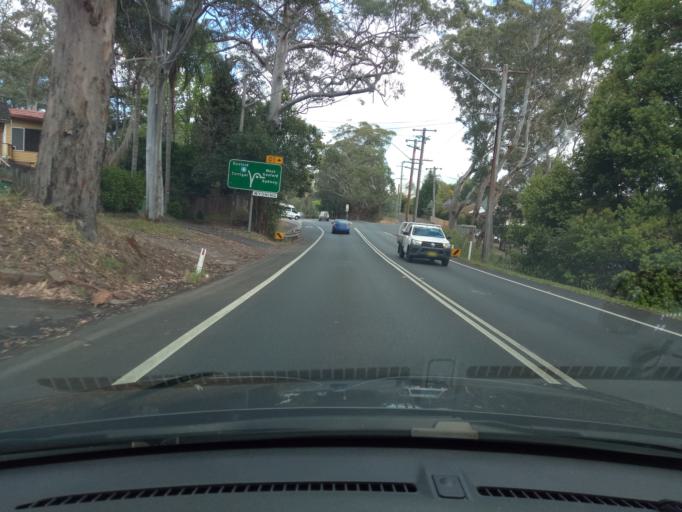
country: AU
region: New South Wales
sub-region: Gosford Shire
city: Narara
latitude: -33.3962
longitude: 151.3457
